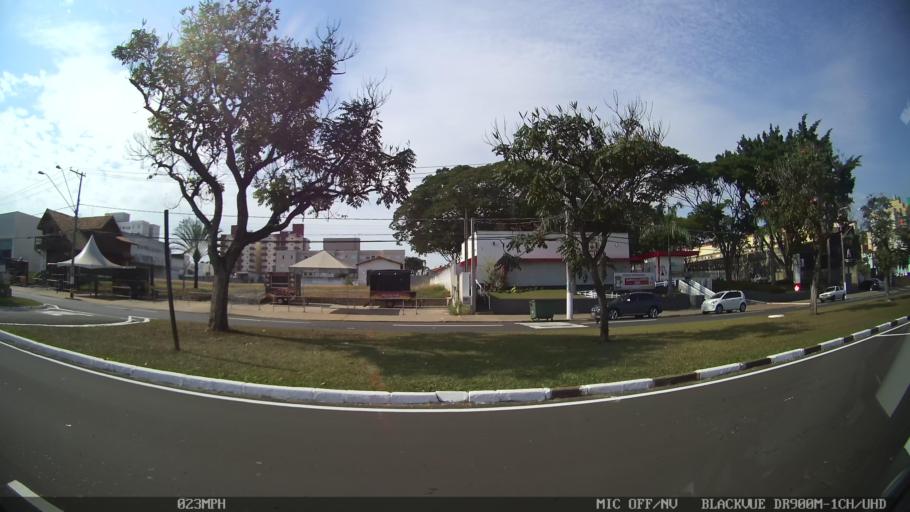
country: BR
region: Sao Paulo
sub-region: Paulinia
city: Paulinia
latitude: -22.7724
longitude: -47.1465
